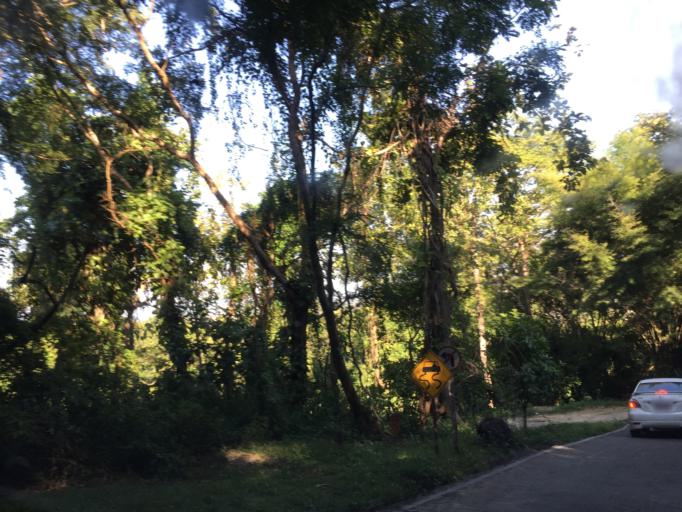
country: TH
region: Chiang Mai
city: Chiang Mai
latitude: 18.8100
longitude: 98.9440
